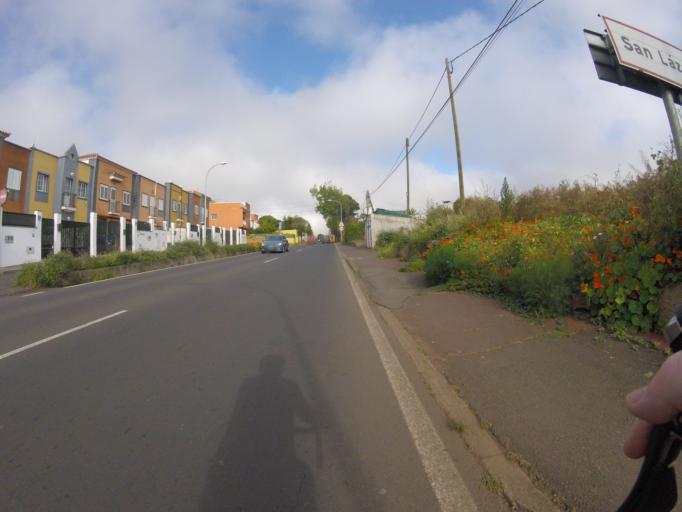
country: ES
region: Canary Islands
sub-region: Provincia de Santa Cruz de Tenerife
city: La Laguna
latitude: 28.4901
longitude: -16.3314
